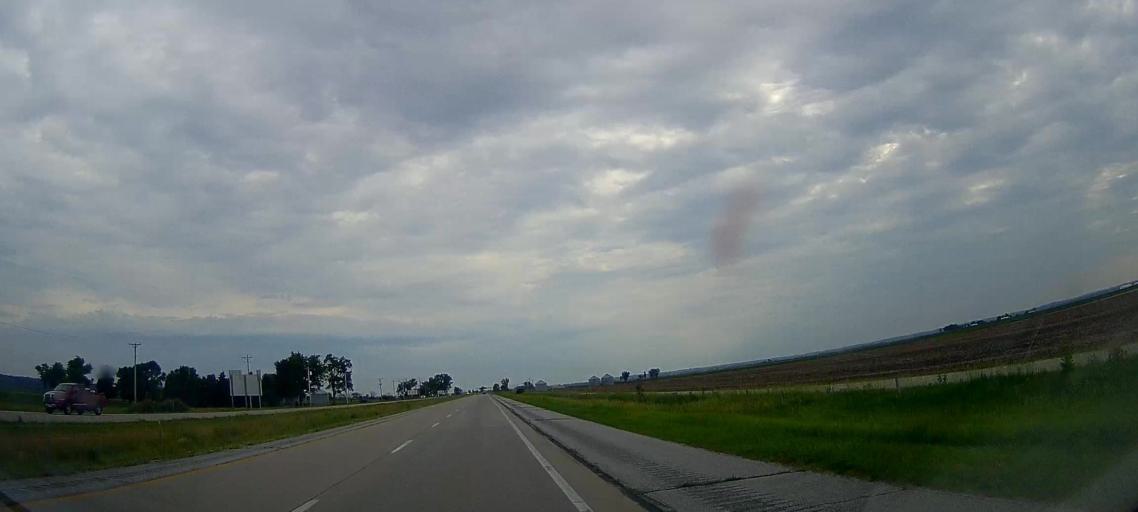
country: US
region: Iowa
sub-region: Harrison County
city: Missouri Valley
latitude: 41.5330
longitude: -95.9179
